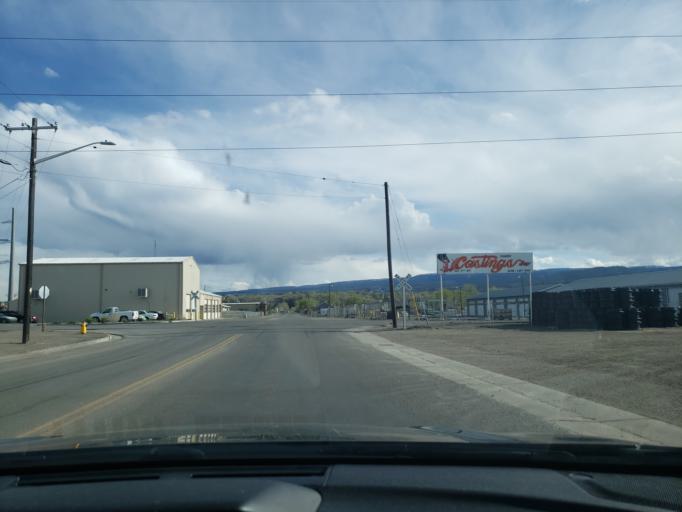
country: US
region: Colorado
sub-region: Mesa County
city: Grand Junction
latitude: 39.0597
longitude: -108.5577
